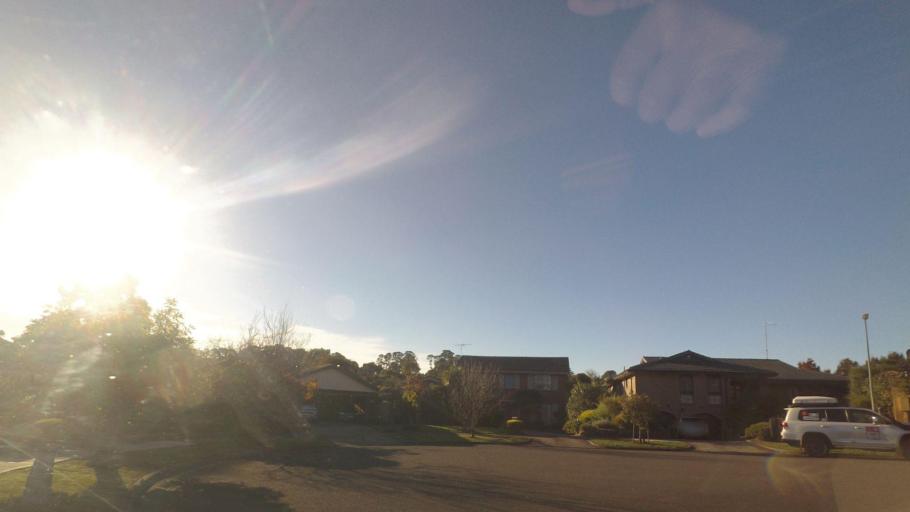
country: AU
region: Victoria
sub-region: Manningham
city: Doncaster East
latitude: -37.7804
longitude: 145.1497
